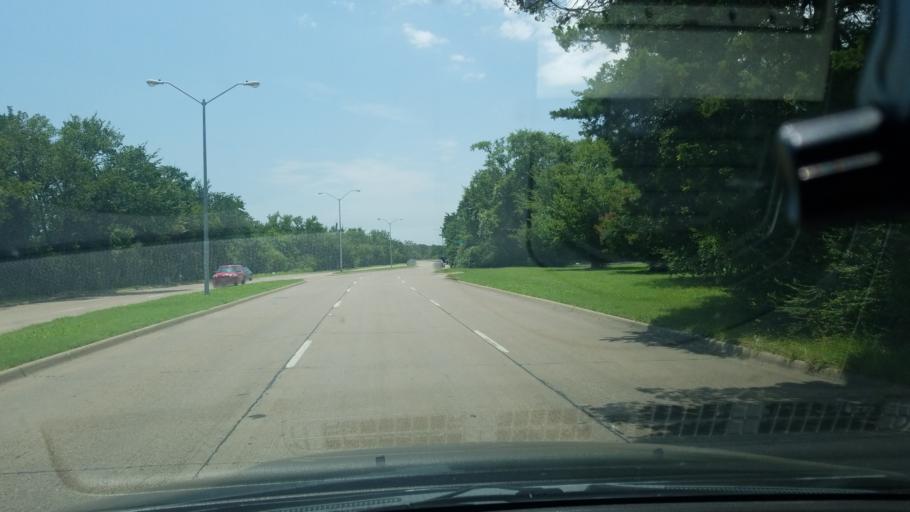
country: US
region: Texas
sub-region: Dallas County
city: Balch Springs
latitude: 32.7279
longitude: -96.6657
